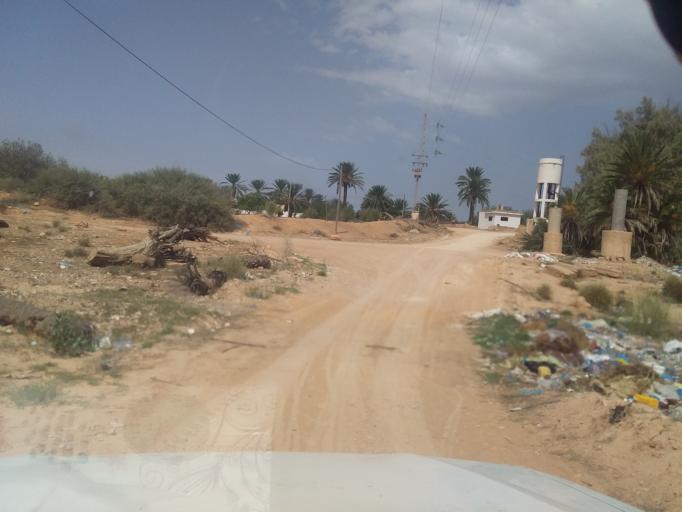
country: TN
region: Madanin
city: Medenine
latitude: 33.5959
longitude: 10.3246
